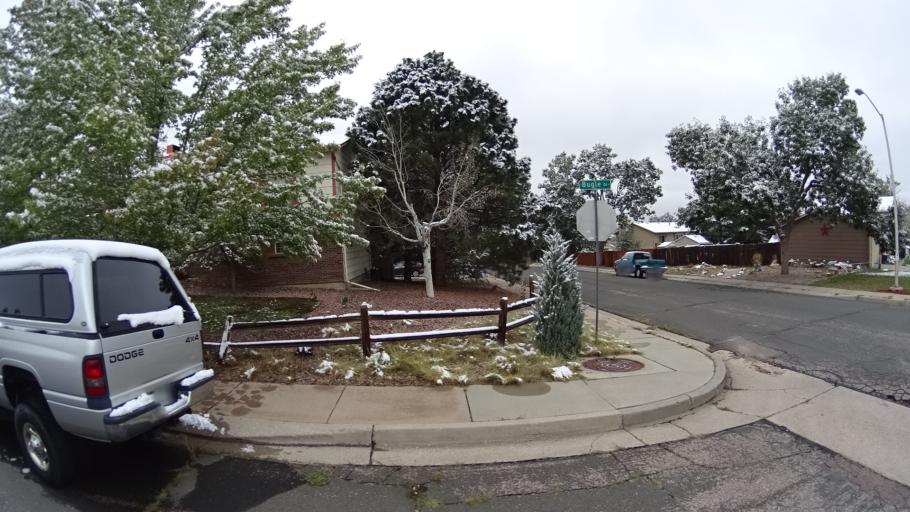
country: US
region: Colorado
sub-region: El Paso County
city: Cimarron Hills
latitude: 38.9269
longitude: -104.7696
